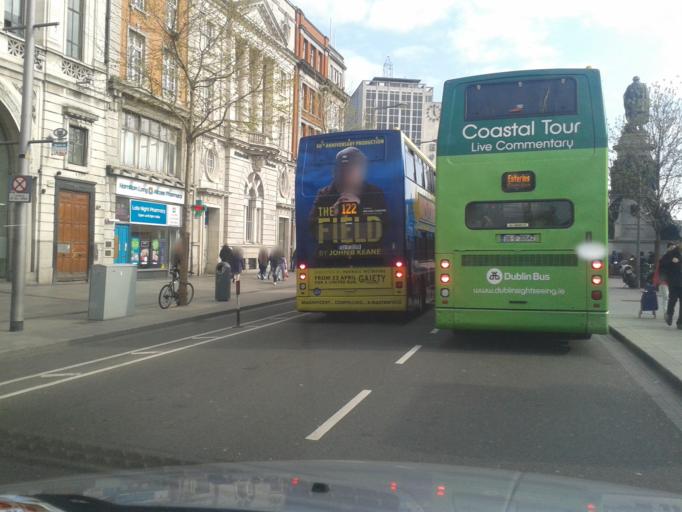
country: IE
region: Leinster
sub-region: Dublin City
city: Dublin
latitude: 53.3481
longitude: -6.2594
